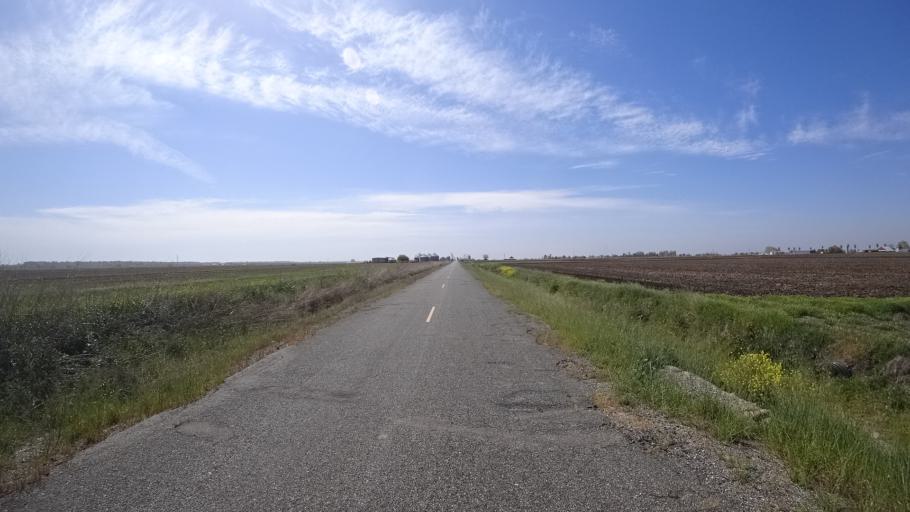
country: US
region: California
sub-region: Glenn County
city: Hamilton City
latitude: 39.5981
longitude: -122.0276
